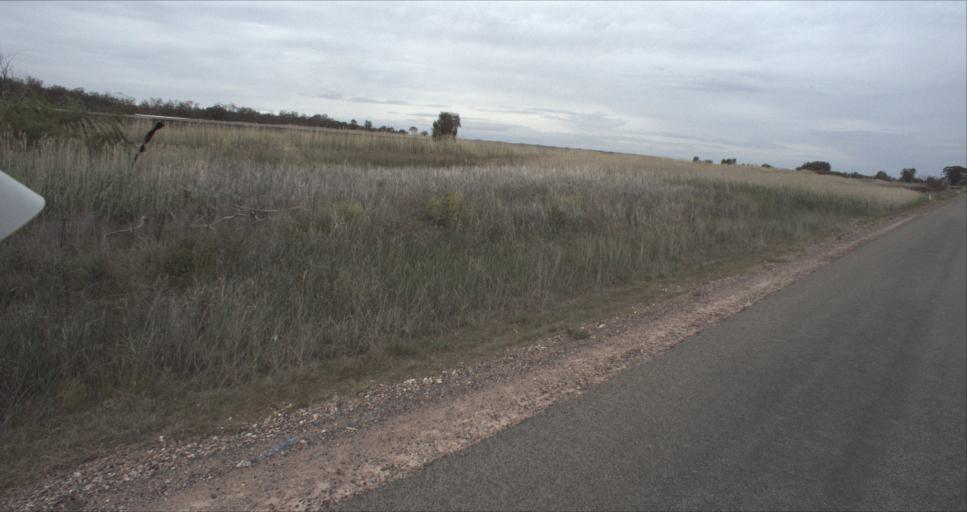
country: AU
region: New South Wales
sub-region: Leeton
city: Leeton
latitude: -34.4312
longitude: 146.3773
